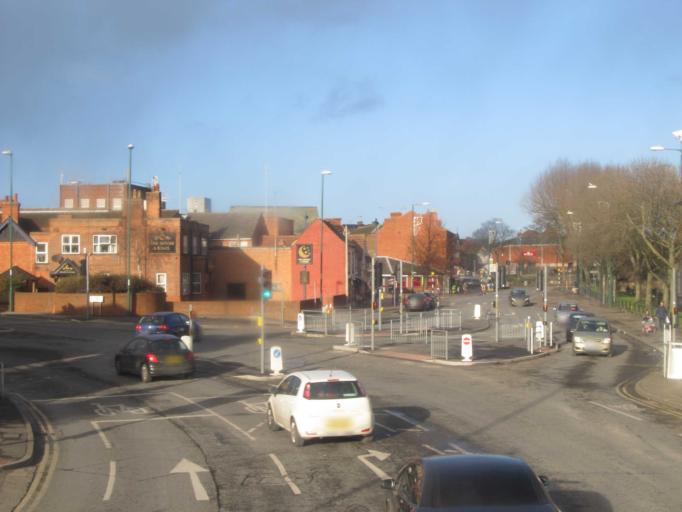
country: GB
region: England
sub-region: Nottinghamshire
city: Hucknall
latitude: 52.9987
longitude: -1.1971
